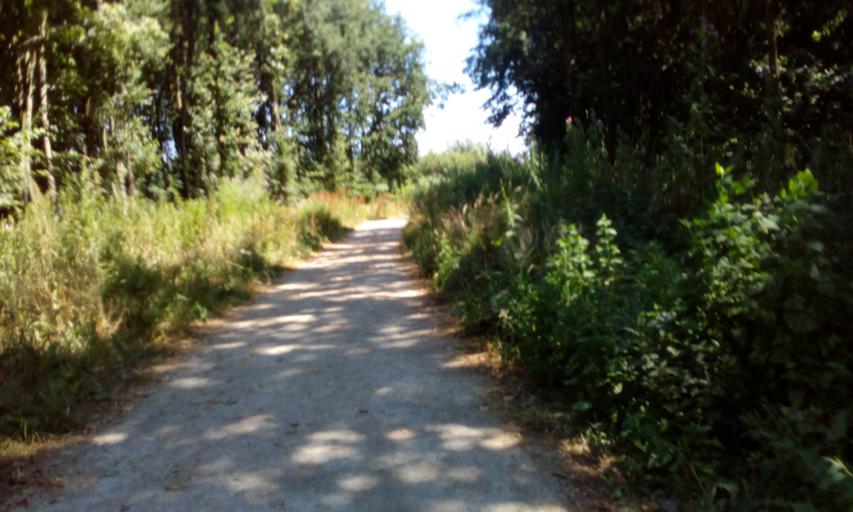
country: NL
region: South Holland
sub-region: Gemeente Pijnacker-Nootdorp
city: Pijnacker
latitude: 52.0336
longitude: 4.4197
